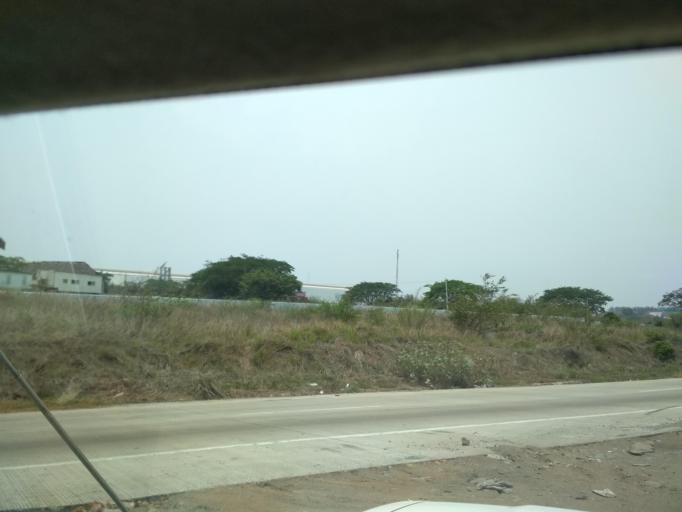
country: MX
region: Veracruz
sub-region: Veracruz
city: Oasis
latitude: 19.1915
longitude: -96.2453
